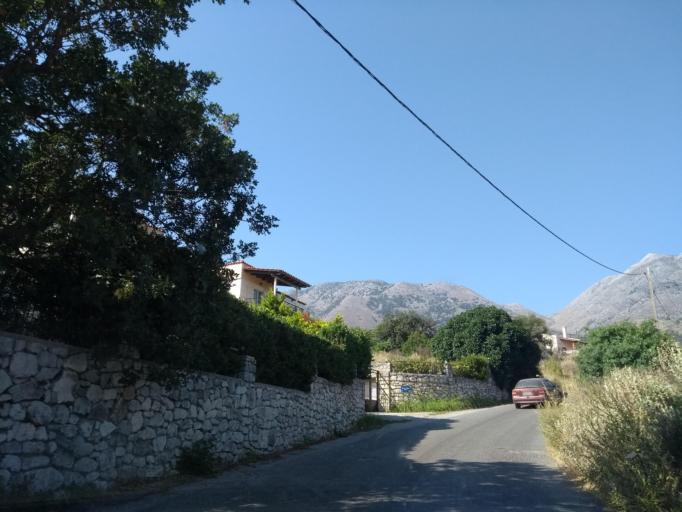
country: GR
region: Crete
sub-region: Nomos Chanias
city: Georgioupolis
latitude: 35.3202
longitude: 24.2981
